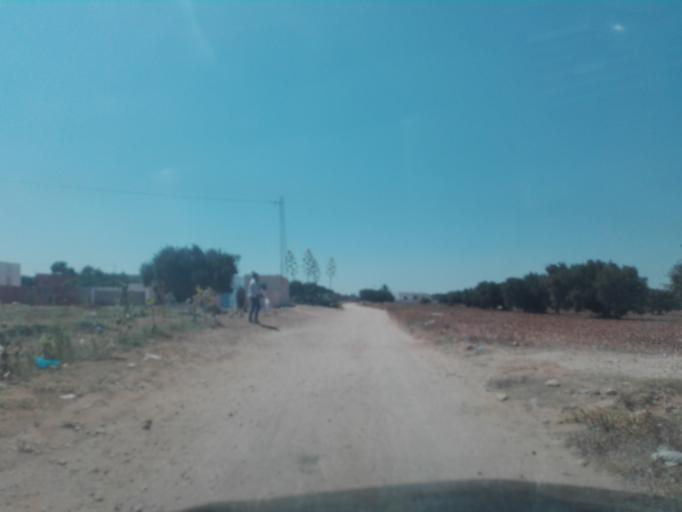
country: TN
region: Safaqis
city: Jabinyanah
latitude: 35.1071
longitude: 10.9082
